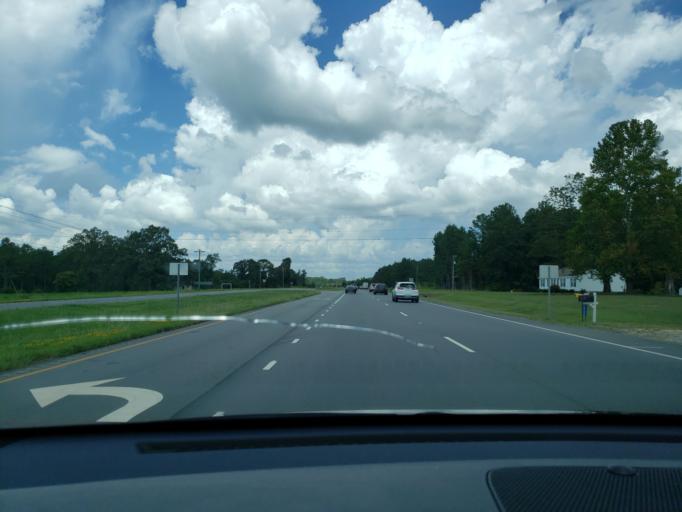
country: US
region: North Carolina
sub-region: Robeson County
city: Saint Pauls
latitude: 34.7760
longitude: -78.8102
